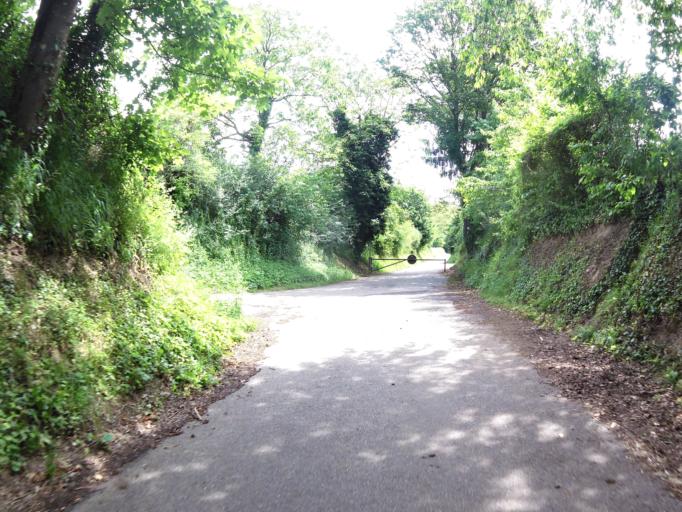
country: DE
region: Baden-Wuerttemberg
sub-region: Freiburg Region
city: Lahr
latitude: 48.3485
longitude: 7.8628
